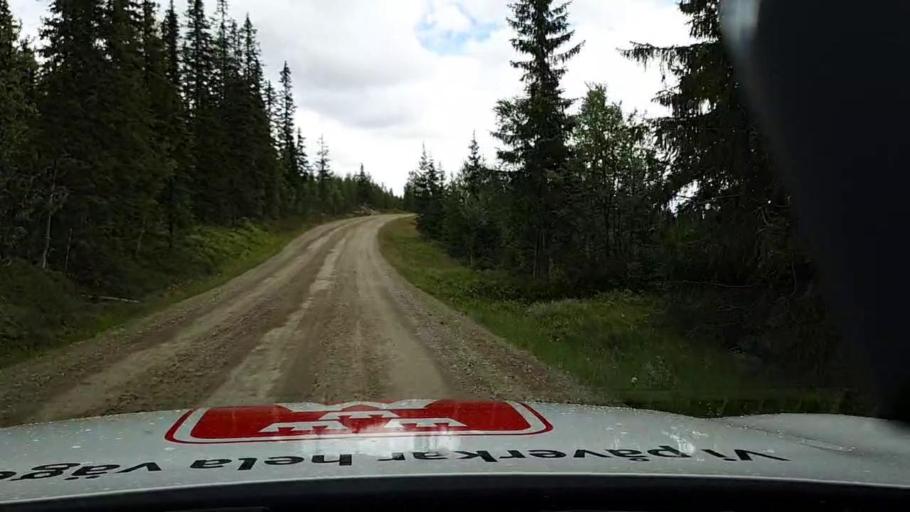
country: SE
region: Jaemtland
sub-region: Are Kommun
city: Jarpen
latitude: 62.6003
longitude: 13.2344
